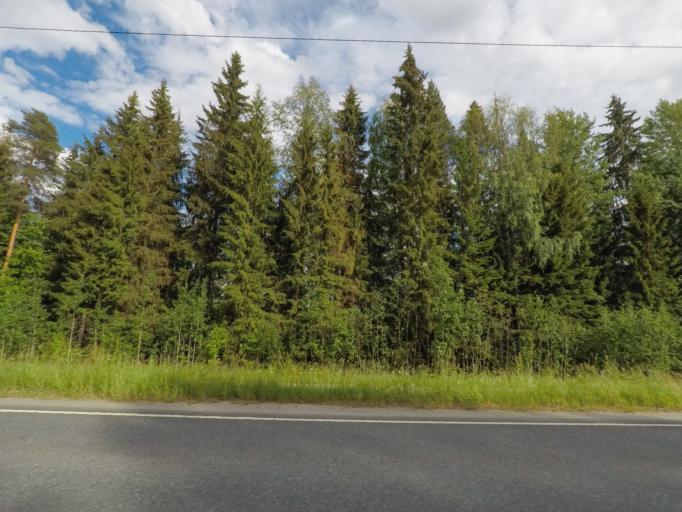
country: FI
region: Paijanne Tavastia
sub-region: Lahti
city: Lahti
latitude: 60.9511
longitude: 25.6120
